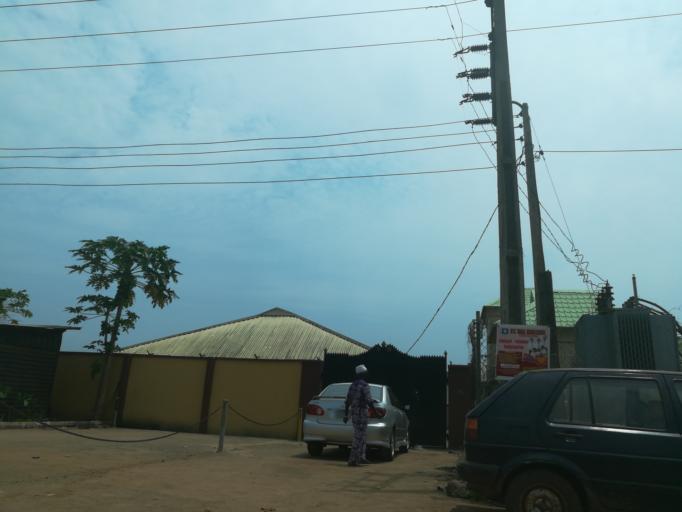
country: NG
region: Lagos
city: Ikorodu
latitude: 6.6078
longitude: 3.5926
